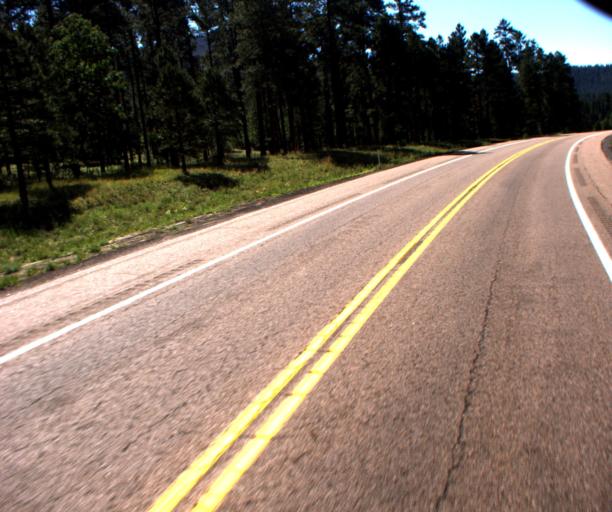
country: US
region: Arizona
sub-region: Apache County
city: Eagar
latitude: 33.8976
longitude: -109.1558
